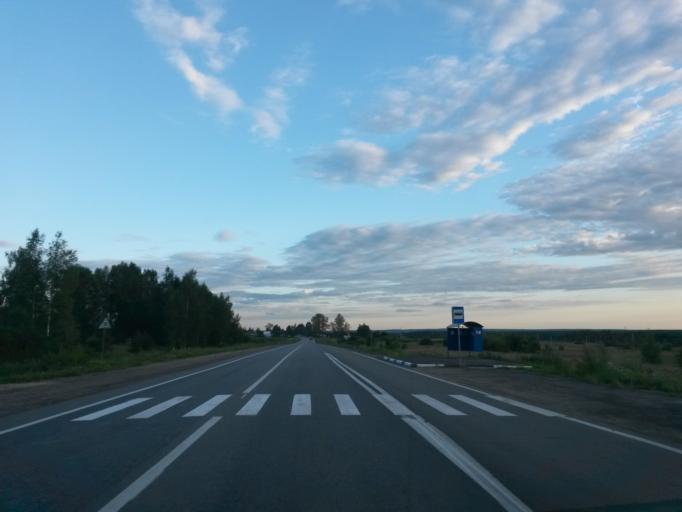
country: RU
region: Jaroslavl
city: Gavrilov-Yam
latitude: 57.3588
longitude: 39.9082
